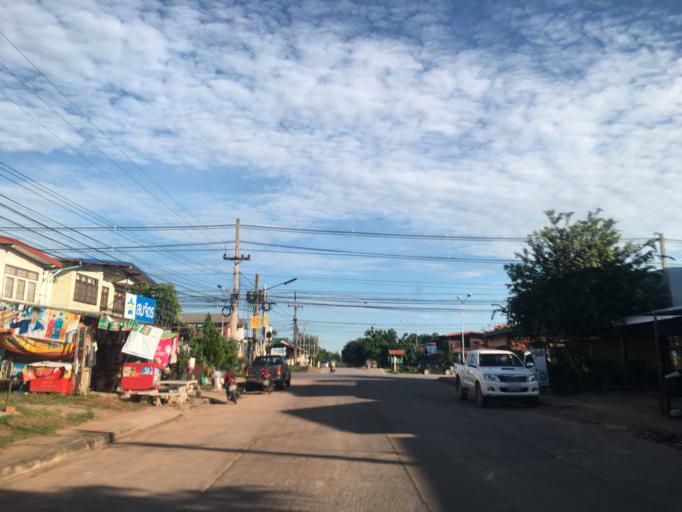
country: TH
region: Changwat Udon Thani
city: Kut Chap
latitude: 17.3220
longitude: 102.6489
